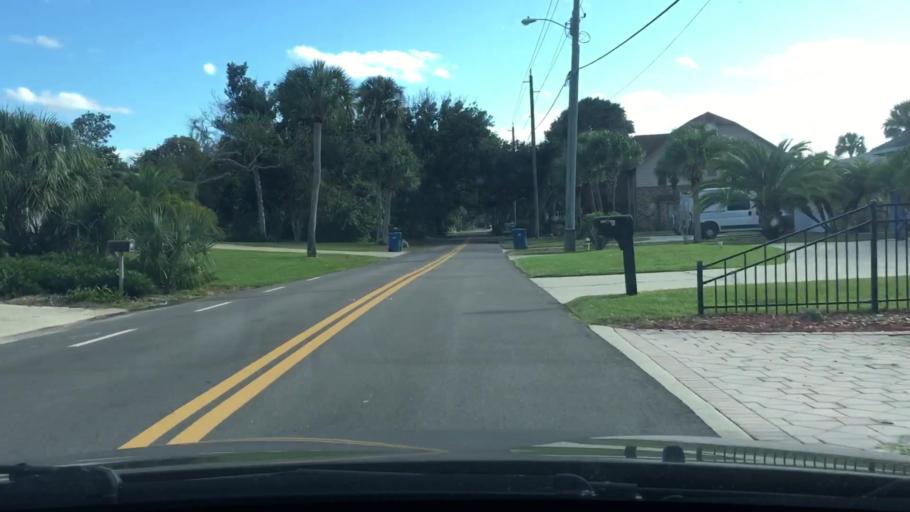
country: US
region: Florida
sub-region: Volusia County
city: Ormond-by-the-Sea
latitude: 29.3784
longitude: -81.0854
